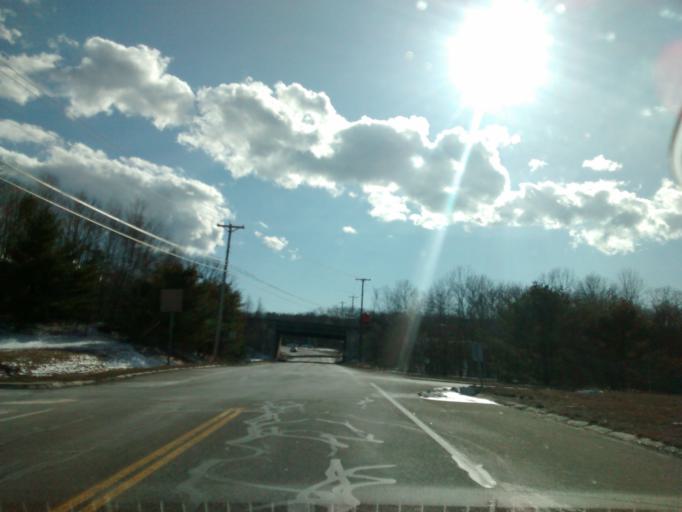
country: US
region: Massachusetts
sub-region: Worcester County
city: Uxbridge
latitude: 42.0680
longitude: -71.6647
